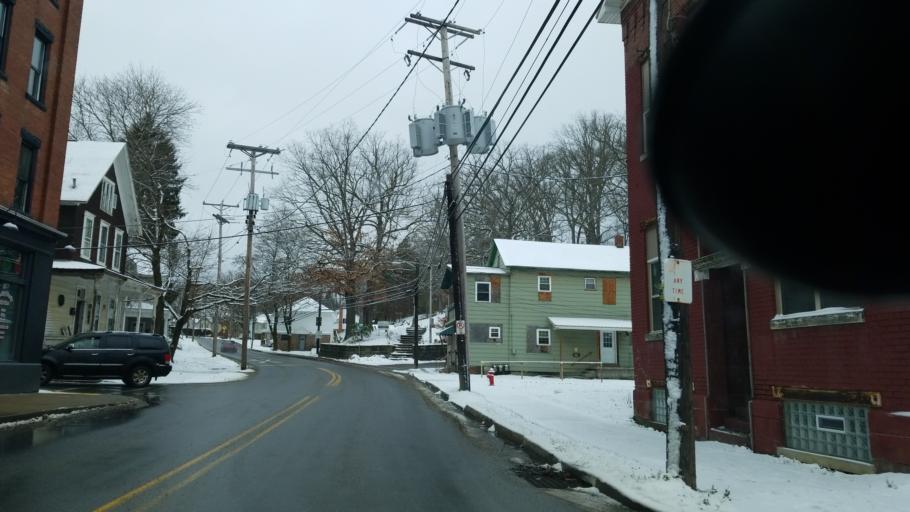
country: US
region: Pennsylvania
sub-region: Jefferson County
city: Punxsutawney
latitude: 40.9460
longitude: -78.9722
